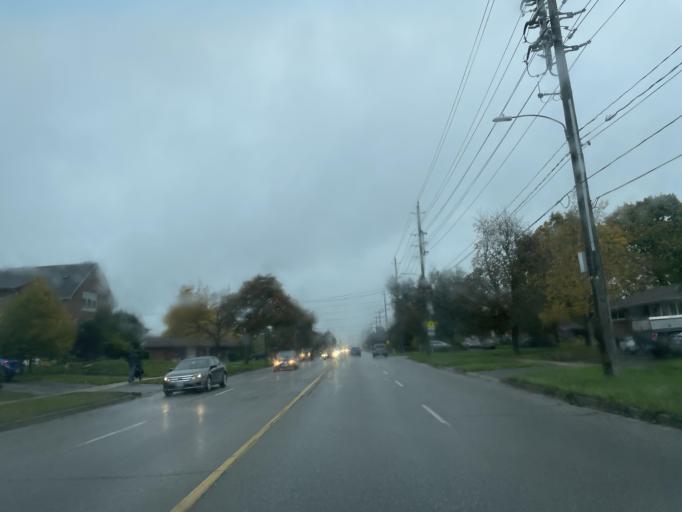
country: CA
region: Ontario
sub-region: Wellington County
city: Guelph
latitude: 43.5609
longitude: -80.2365
